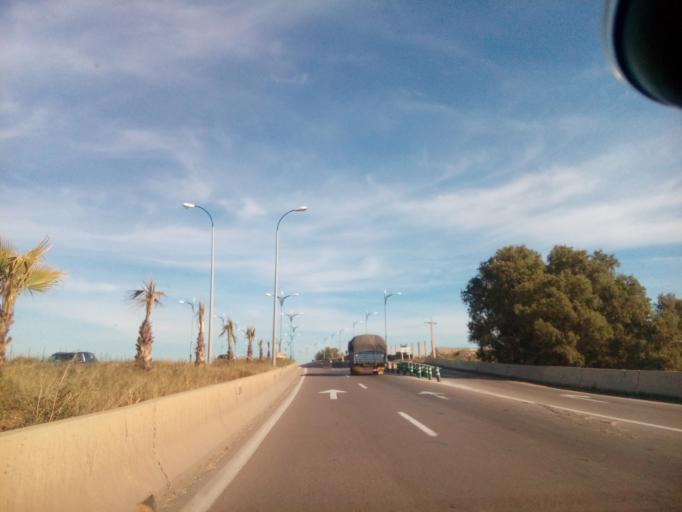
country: DZ
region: Mostaganem
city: Mostaganem
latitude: 35.8874
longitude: 0.0549
